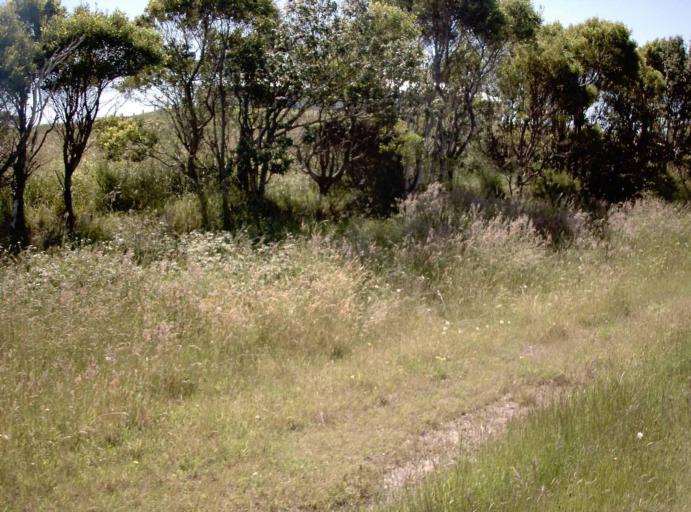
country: AU
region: Victoria
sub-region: Latrobe
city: Morwell
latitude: -38.6841
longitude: 146.1467
